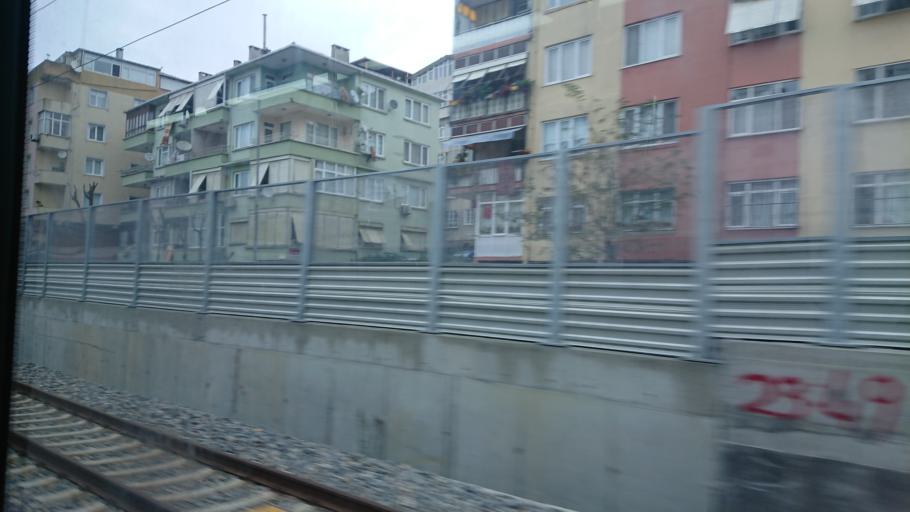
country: TR
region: Istanbul
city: Mahmutbey
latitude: 40.9978
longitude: 28.7675
